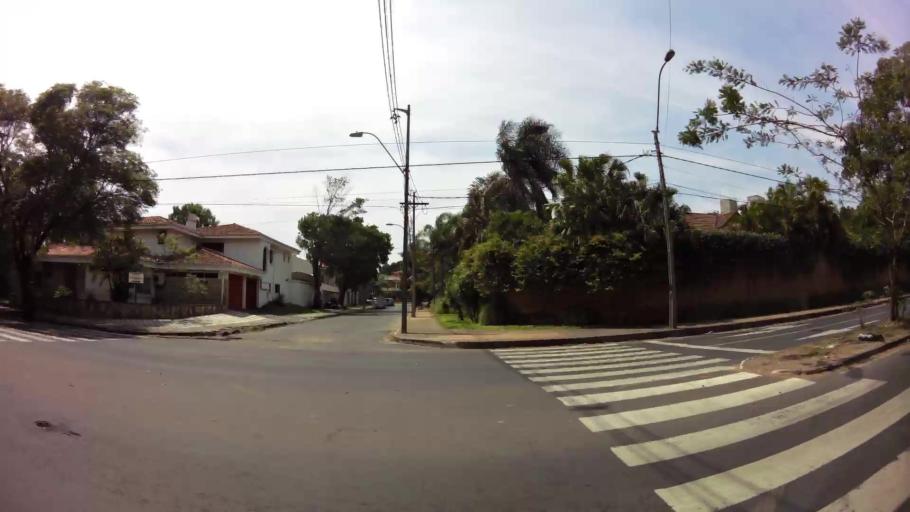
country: PY
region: Asuncion
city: Asuncion
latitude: -25.2841
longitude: -57.5880
